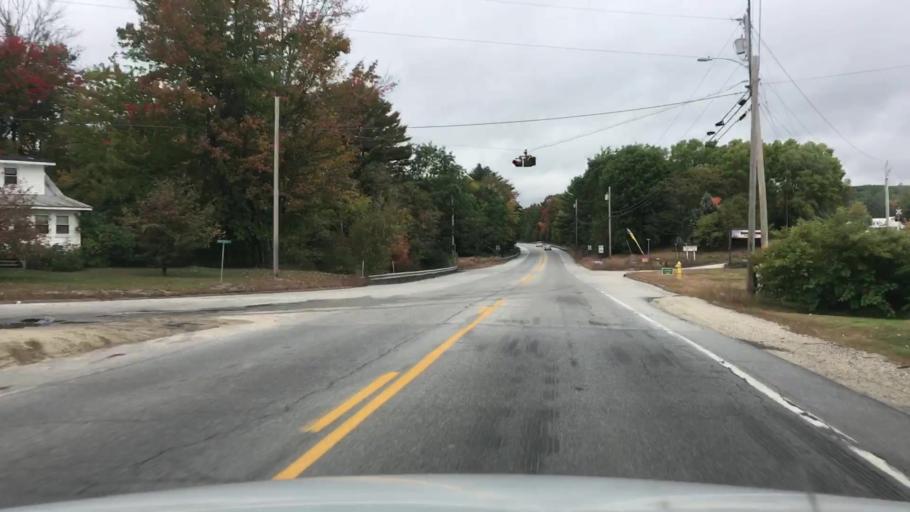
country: US
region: Maine
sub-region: Oxford County
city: Oxford
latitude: 44.1633
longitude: -70.4987
